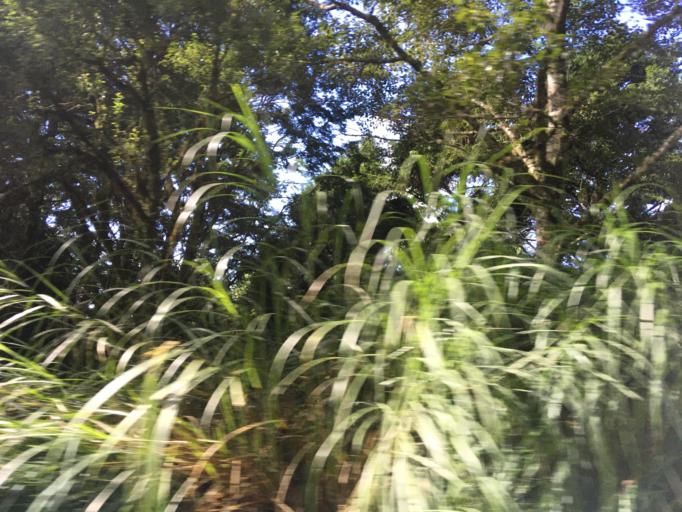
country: TW
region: Taiwan
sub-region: Yilan
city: Yilan
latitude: 24.5128
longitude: 121.5872
